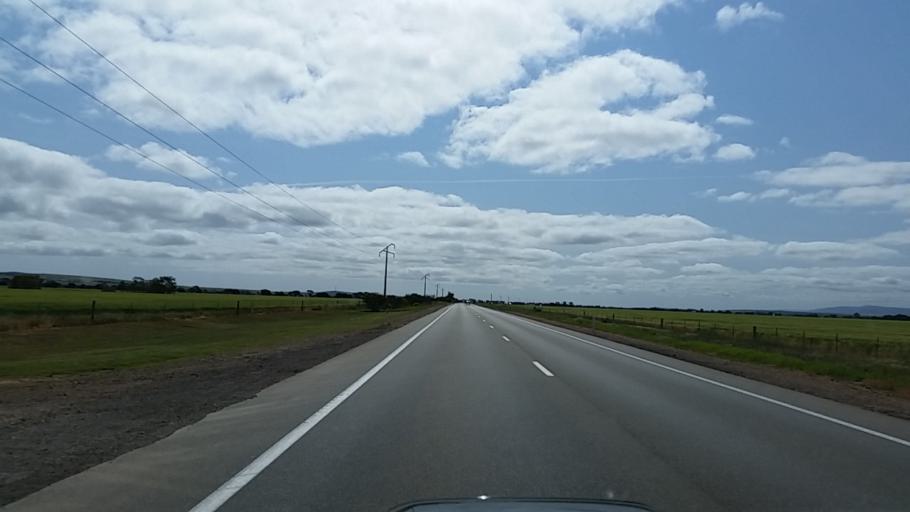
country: AU
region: South Australia
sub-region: Port Pirie City and Dists
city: Crystal Brook
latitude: -33.4778
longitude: 138.1696
